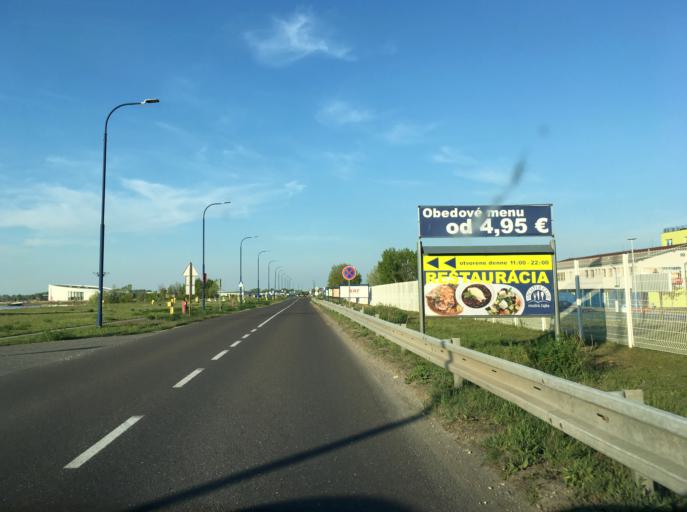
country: HU
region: Gyor-Moson-Sopron
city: Rajka
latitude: 48.0312
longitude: 17.2281
